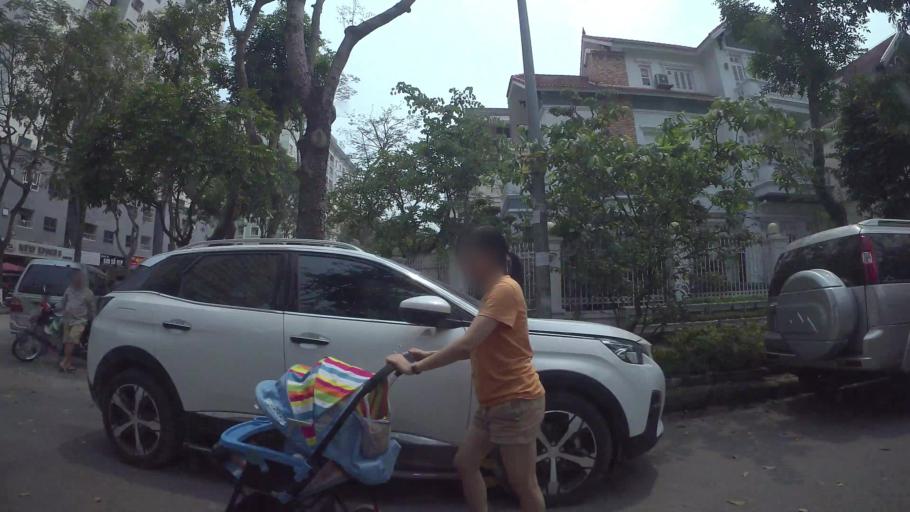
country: VN
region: Ha Noi
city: Van Dien
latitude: 20.9626
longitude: 105.8315
